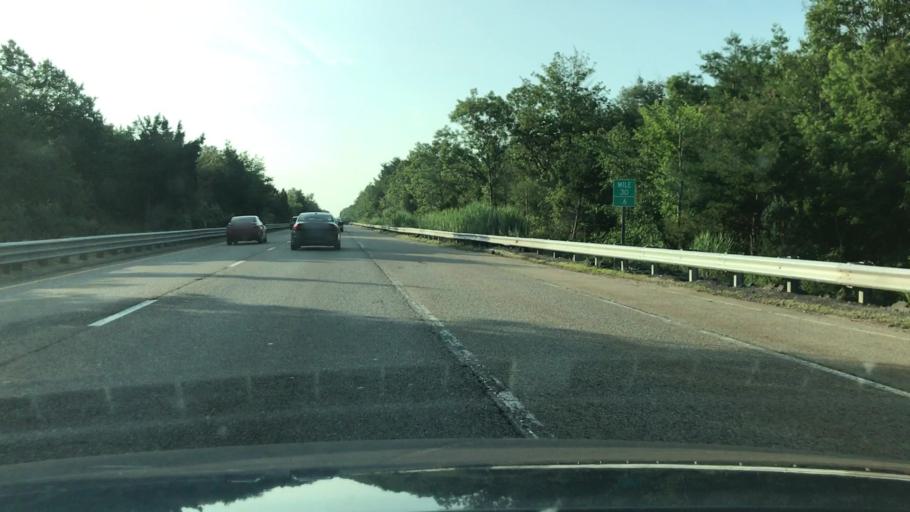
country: US
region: Massachusetts
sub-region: Plymouth County
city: Hanover
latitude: 42.1409
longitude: -70.8262
